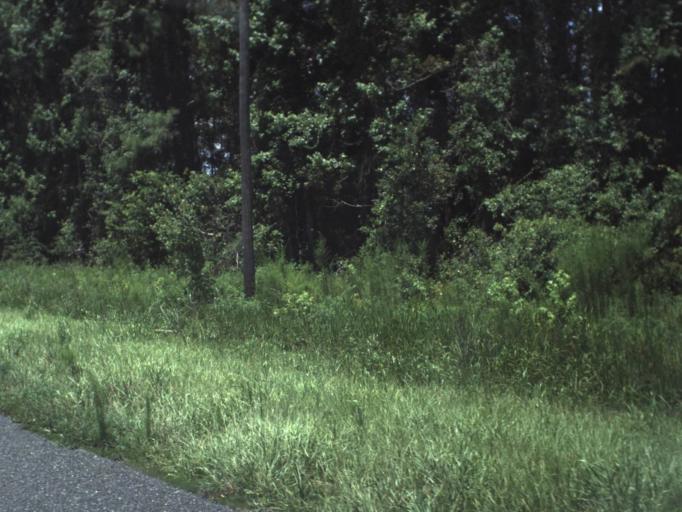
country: US
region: Florida
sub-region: Taylor County
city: Perry
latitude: 30.2923
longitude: -83.7380
